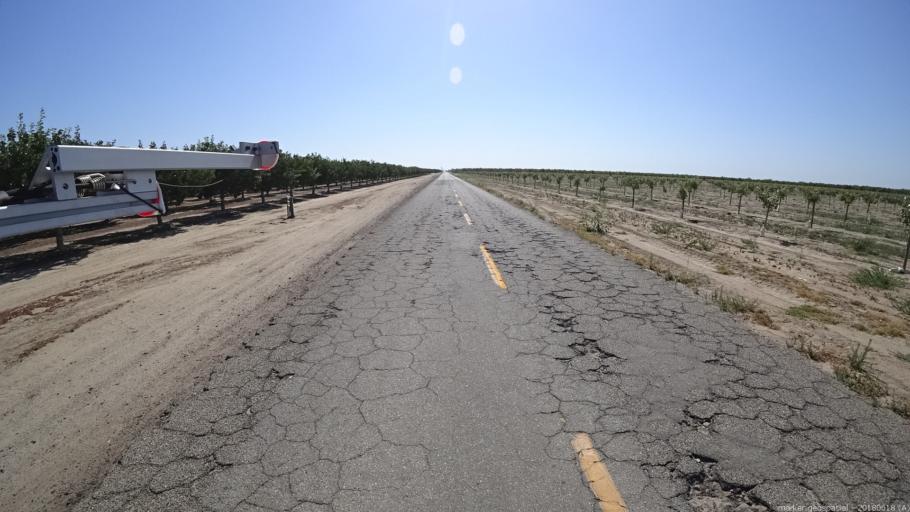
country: US
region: California
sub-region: Fresno County
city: Mendota
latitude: 36.8366
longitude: -120.2315
